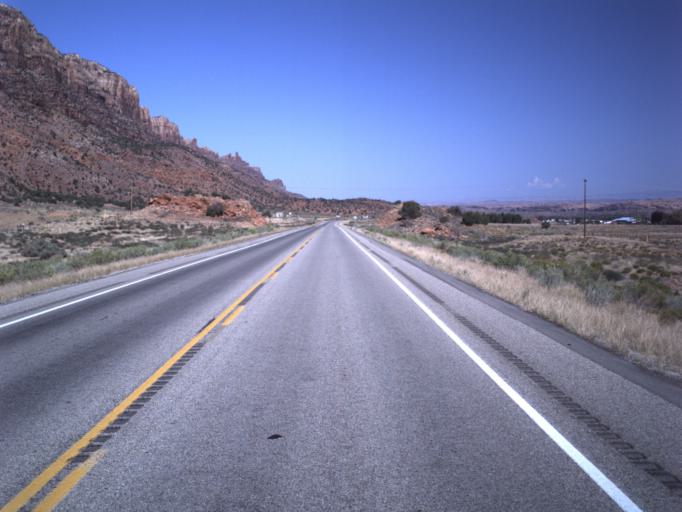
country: US
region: Utah
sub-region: Grand County
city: Moab
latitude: 38.4658
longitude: -109.4491
